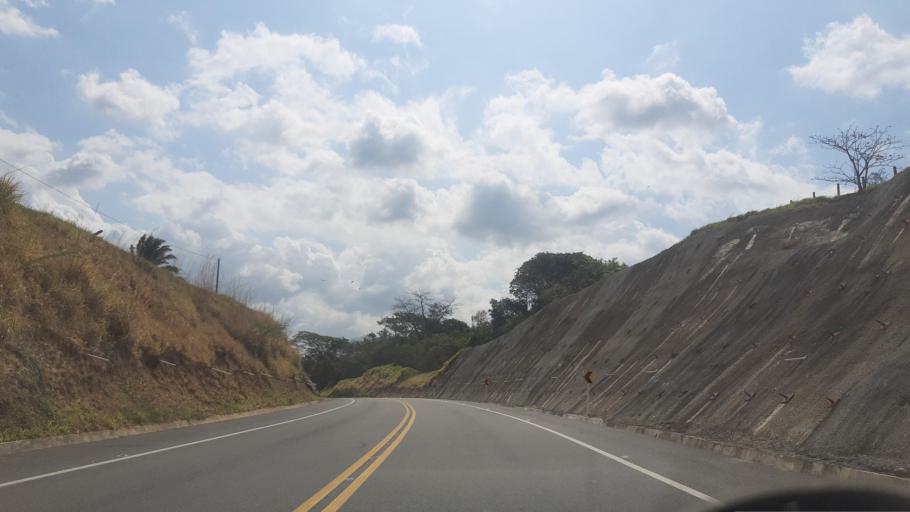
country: CO
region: Casanare
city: Monterrey
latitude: 4.8246
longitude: -72.8089
